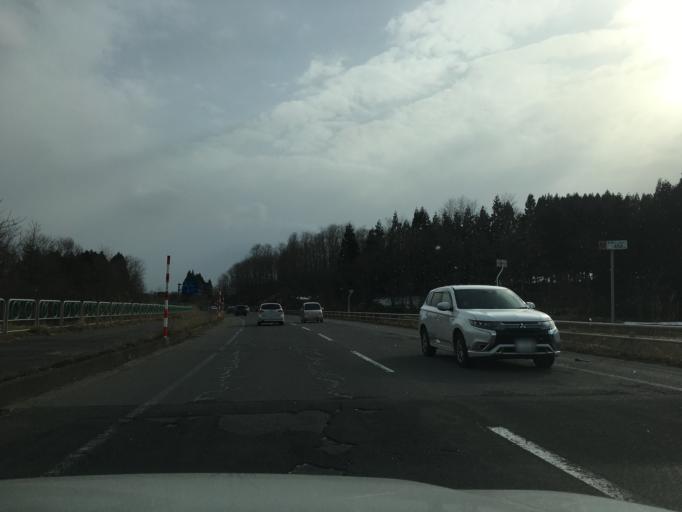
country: JP
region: Aomori
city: Namioka
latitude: 40.7645
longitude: 140.5880
